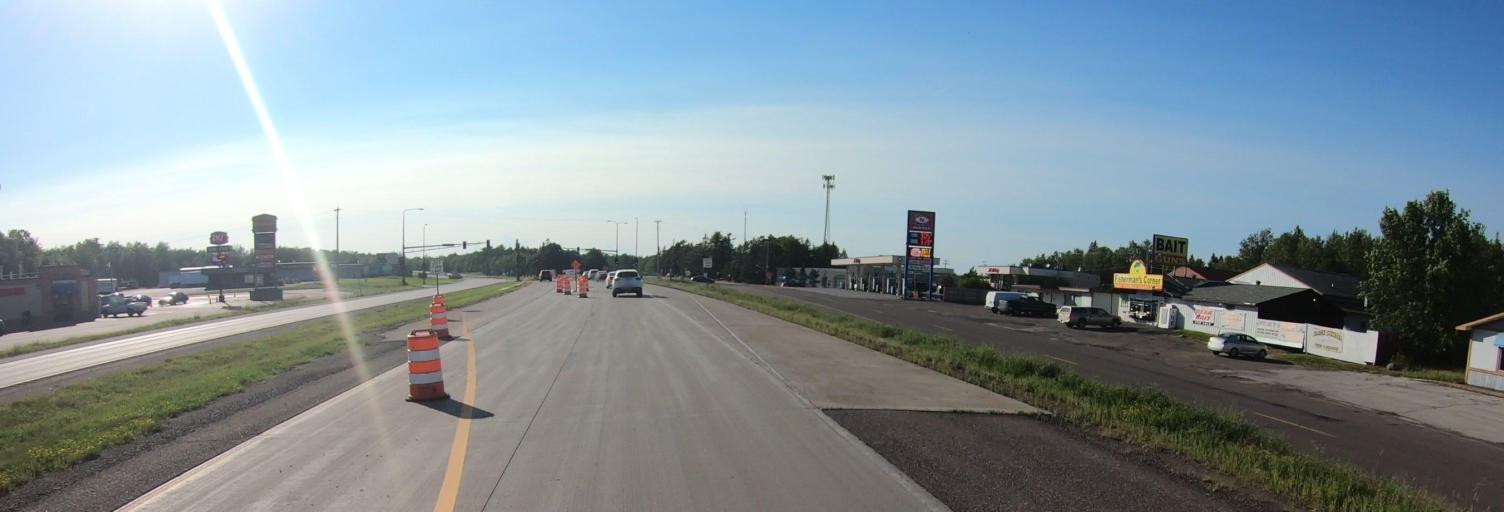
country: US
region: Minnesota
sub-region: Saint Louis County
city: Hermantown
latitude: 46.8498
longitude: -92.2808
